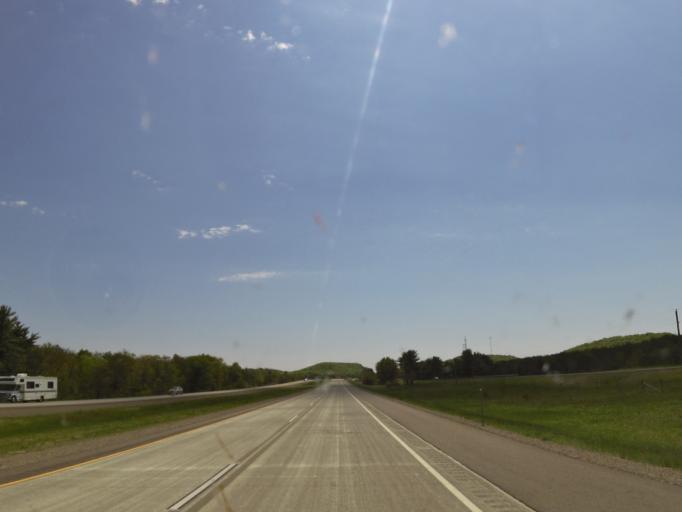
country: US
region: Wisconsin
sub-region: Jackson County
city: Black River Falls
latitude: 44.3474
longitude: -90.9306
